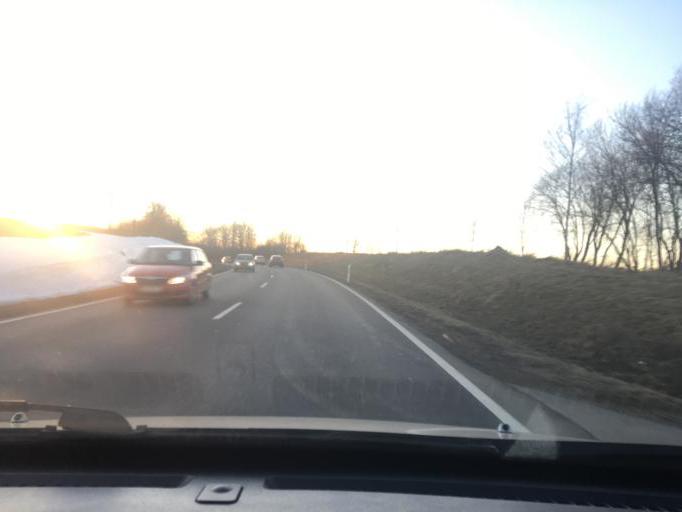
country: DE
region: Baden-Wuerttemberg
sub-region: Tuebingen Region
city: Erlenmoos
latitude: 48.0652
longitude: 9.9995
